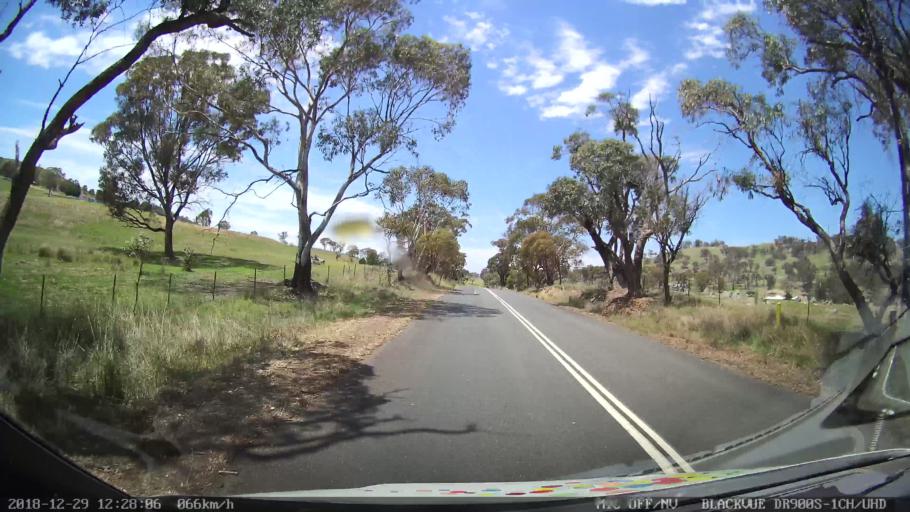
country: AU
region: Australian Capital Territory
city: Macarthur
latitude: -35.4830
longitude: 149.2252
